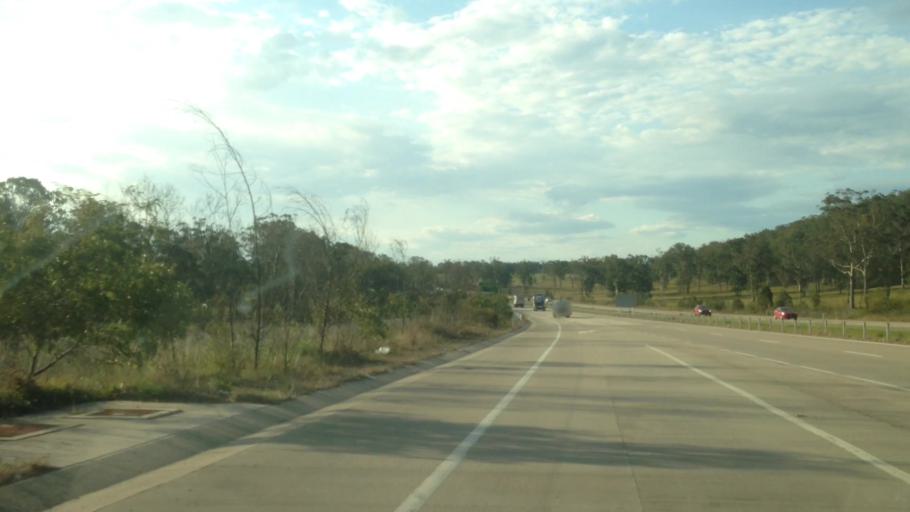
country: AU
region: New South Wales
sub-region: Cessnock
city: Heddon Greta
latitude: -32.8414
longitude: 151.5417
